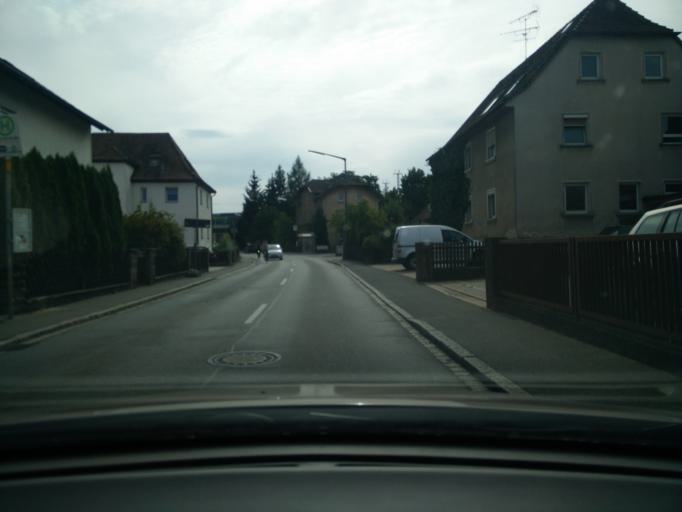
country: DE
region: Bavaria
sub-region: Regierungsbezirk Mittelfranken
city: Veitsbronn
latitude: 49.5076
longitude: 10.8792
